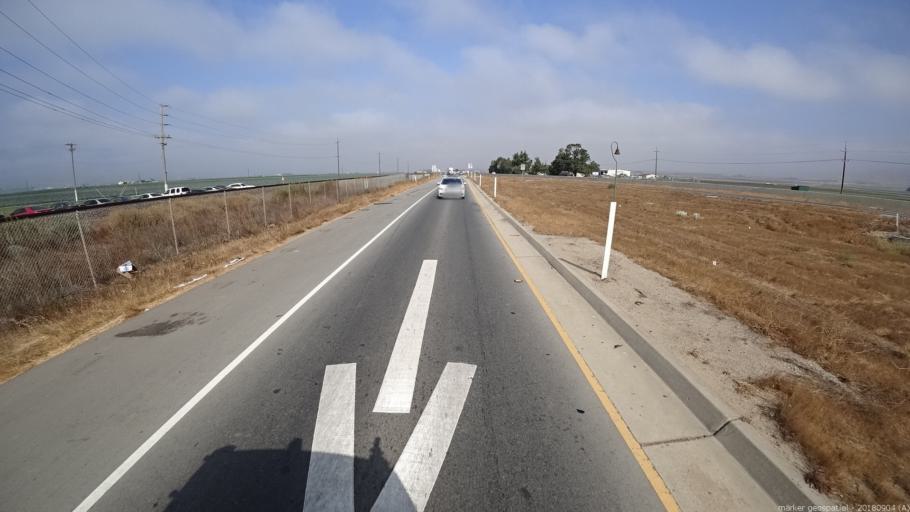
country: US
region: California
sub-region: Monterey County
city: Soledad
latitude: 36.4364
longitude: -121.3445
